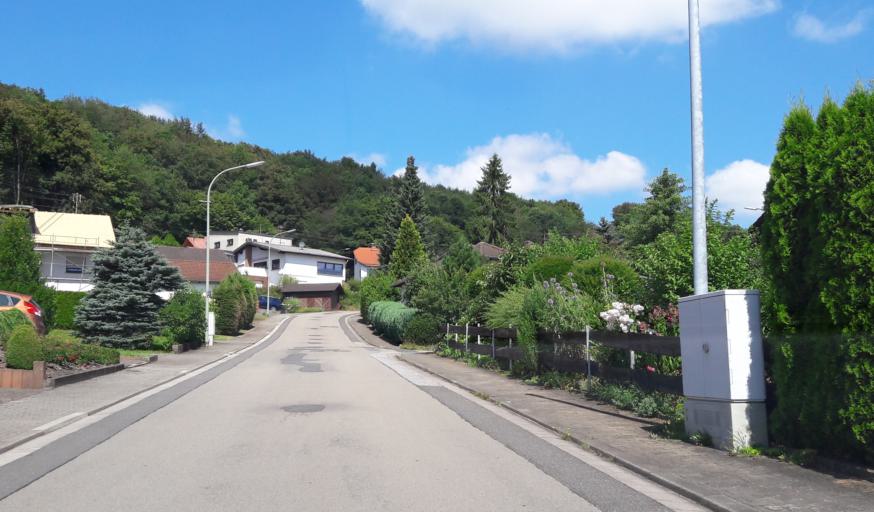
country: DE
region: Saarland
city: Freisen
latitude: 49.5556
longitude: 7.2434
